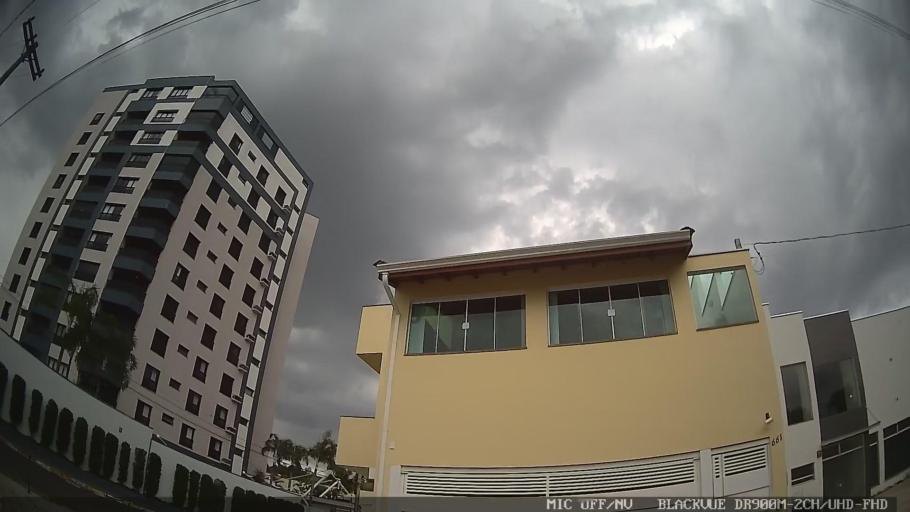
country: BR
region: Sao Paulo
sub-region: Amparo
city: Amparo
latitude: -22.6987
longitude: -46.7608
